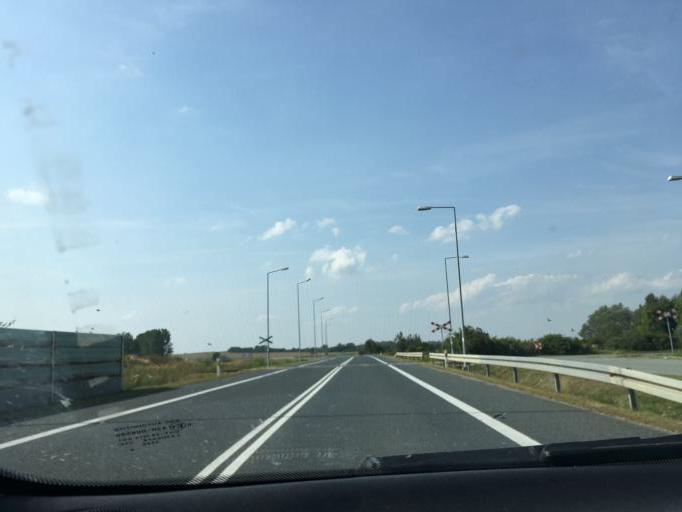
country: PL
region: Opole Voivodeship
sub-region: Powiat prudnicki
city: Prudnik
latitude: 50.3314
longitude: 17.5976
